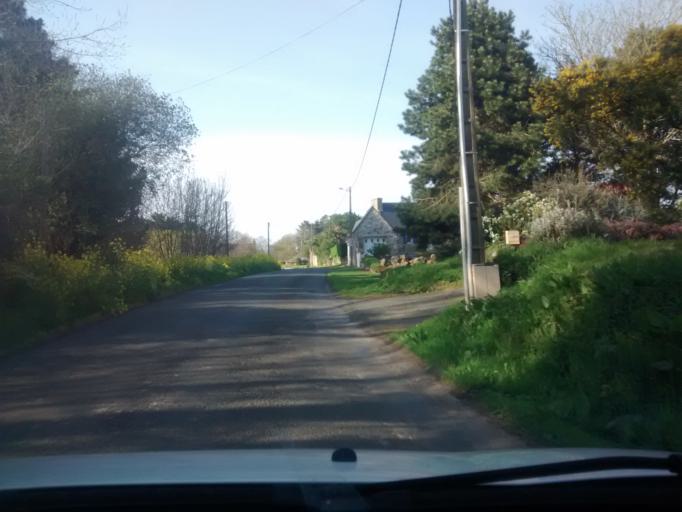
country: FR
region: Brittany
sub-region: Departement des Cotes-d'Armor
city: Penvenan
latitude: 48.8230
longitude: -3.2826
